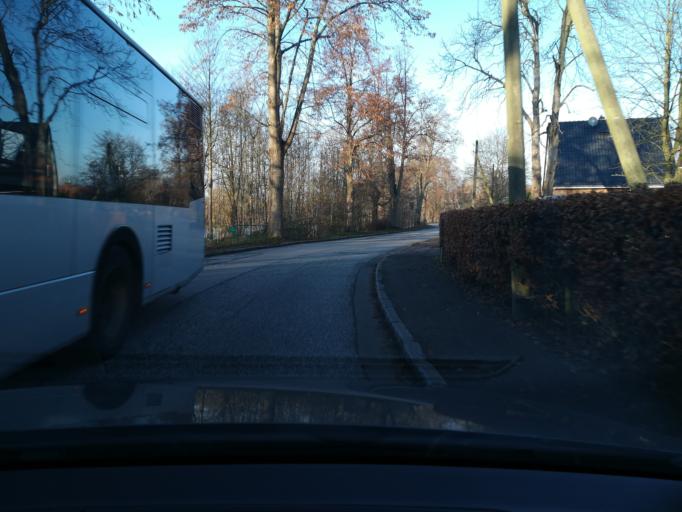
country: DE
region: Lower Saxony
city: Stelle
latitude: 53.4471
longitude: 10.1336
